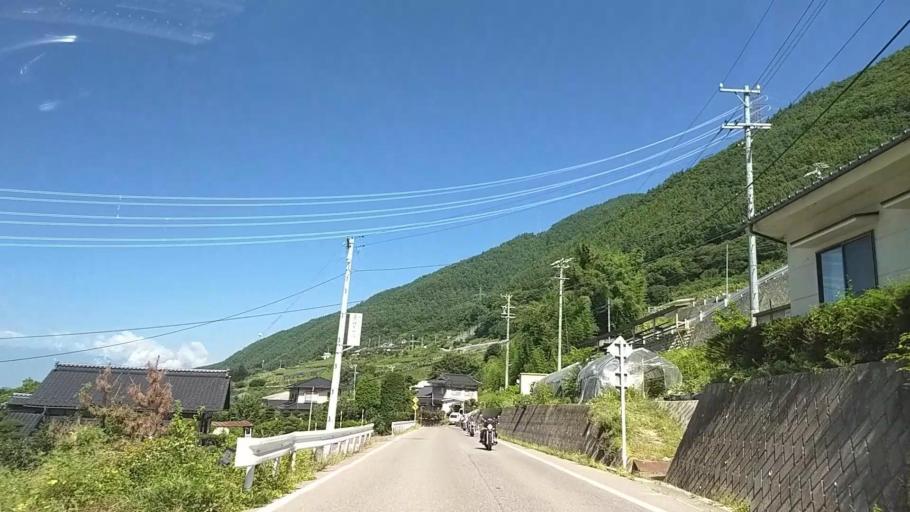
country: JP
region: Nagano
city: Matsumoto
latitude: 36.2219
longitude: 138.0387
